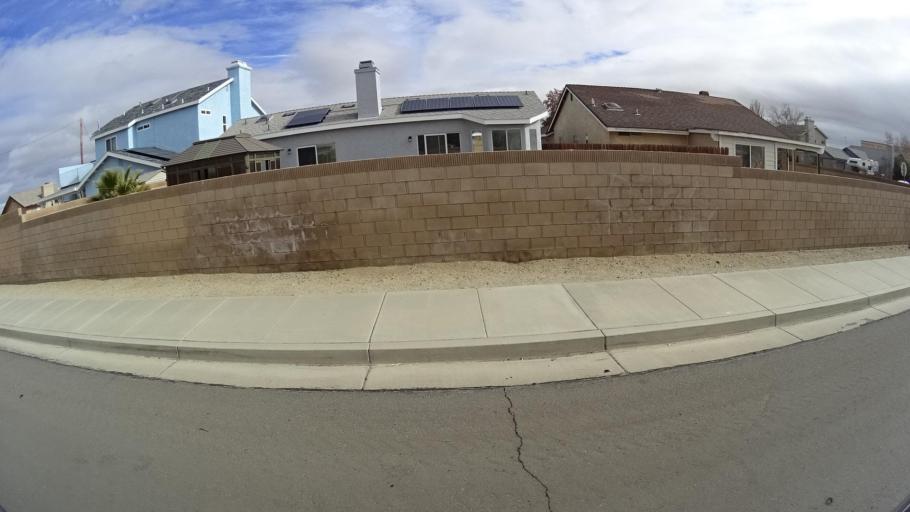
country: US
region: California
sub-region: Kern County
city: Rosamond
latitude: 34.8679
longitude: -118.2291
